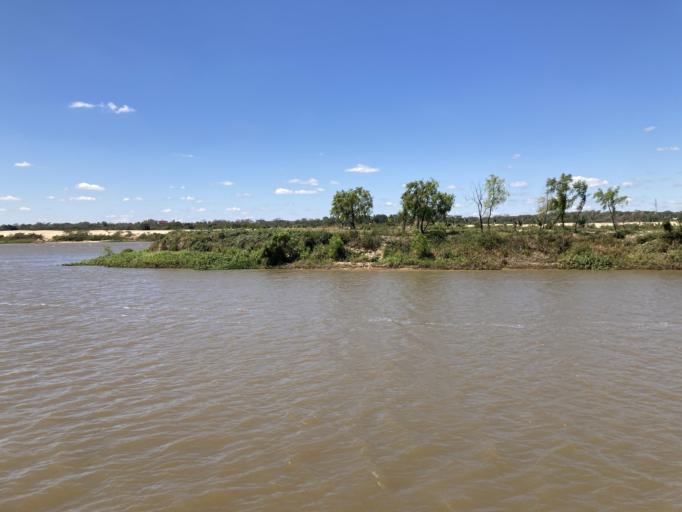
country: PY
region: Central
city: Colonia Mariano Roque Alonso
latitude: -25.1725
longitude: -57.5385
